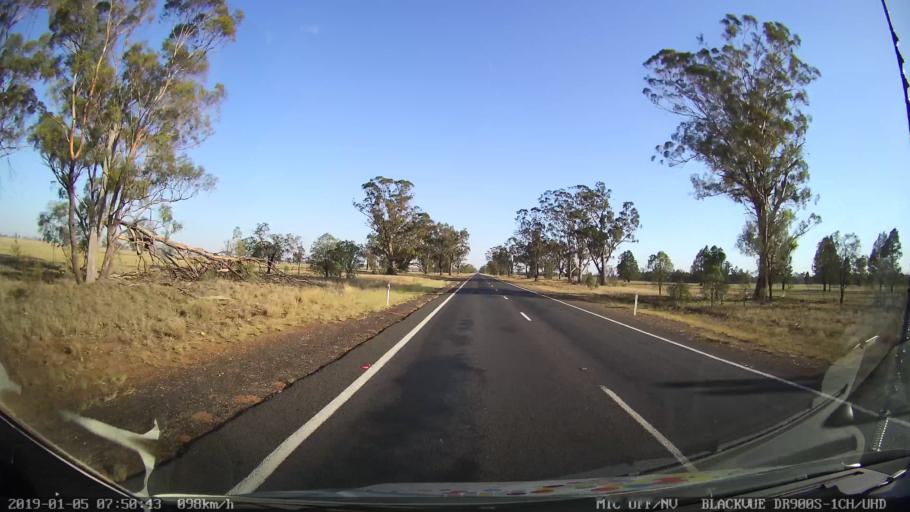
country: AU
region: New South Wales
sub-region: Gilgandra
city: Gilgandra
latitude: -31.7834
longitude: 148.6380
